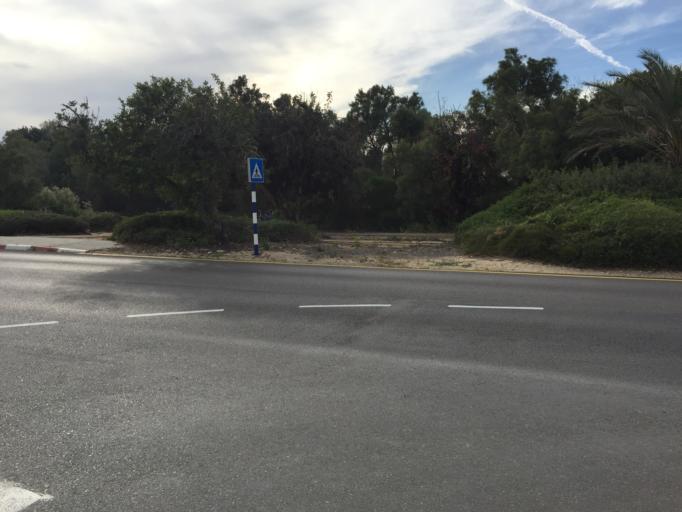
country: IL
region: Haifa
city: Qesarya
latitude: 32.5096
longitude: 34.9046
